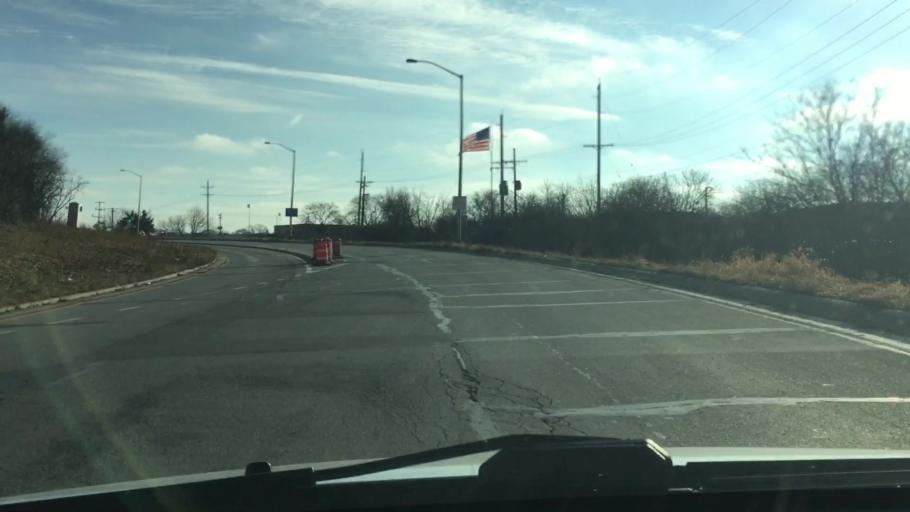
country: US
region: Wisconsin
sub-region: Waukesha County
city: Butler
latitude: 43.0739
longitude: -88.0588
